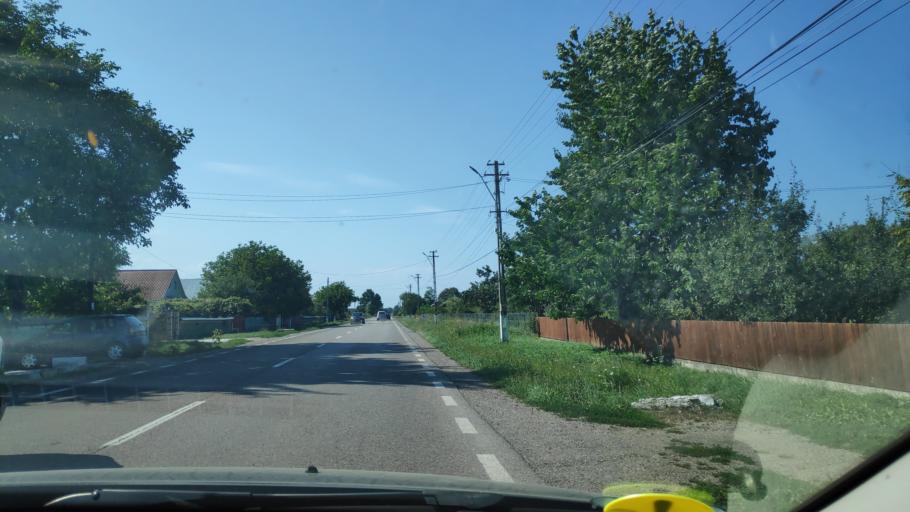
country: RO
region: Suceava
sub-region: Comuna Boroaia
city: Boroaia
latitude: 47.3619
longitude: 26.3396
